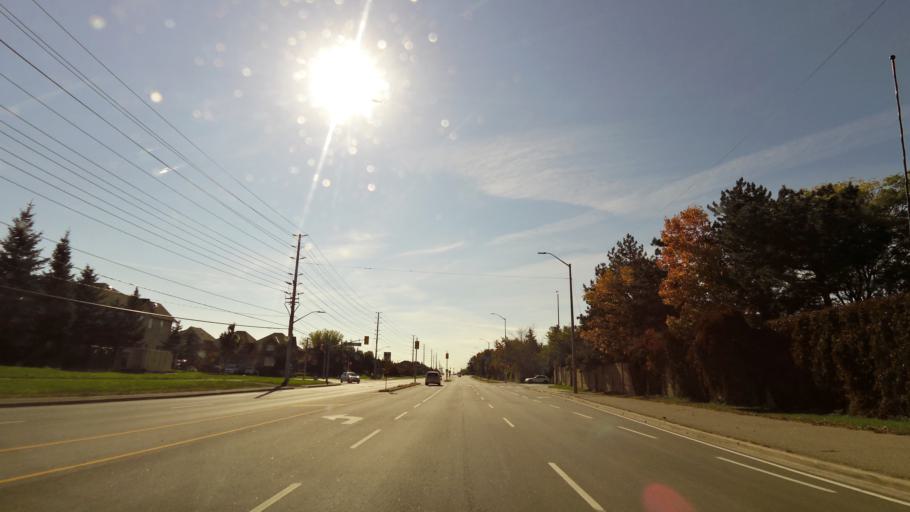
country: CA
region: Ontario
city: Mississauga
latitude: 43.5671
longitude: -79.7462
